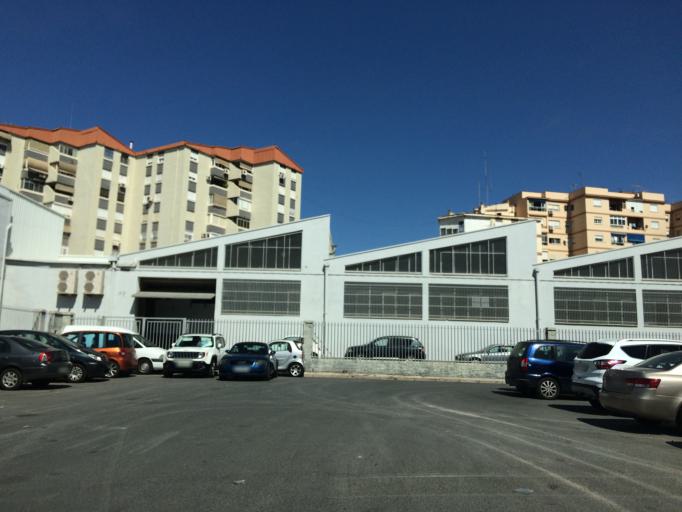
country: ES
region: Andalusia
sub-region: Provincia de Malaga
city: Malaga
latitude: 36.7081
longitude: -4.4463
